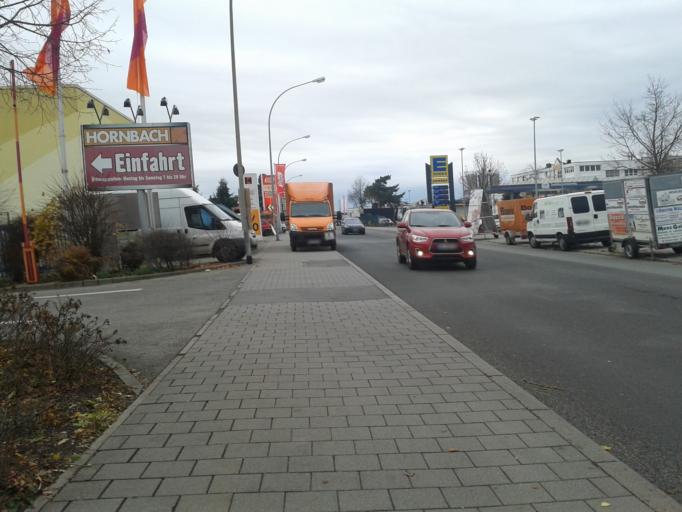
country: DE
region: Bavaria
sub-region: Upper Franconia
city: Hallstadt
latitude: 49.9086
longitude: 10.8786
